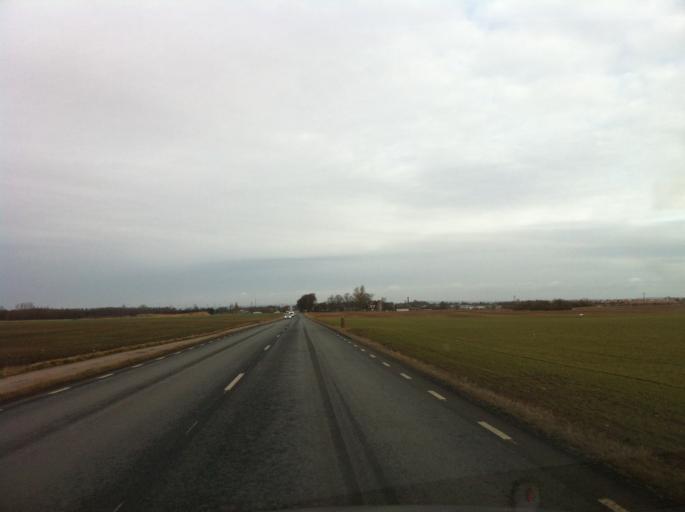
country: SE
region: Skane
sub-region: Angelholms Kommun
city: AEngelholm
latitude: 56.2170
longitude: 12.8575
